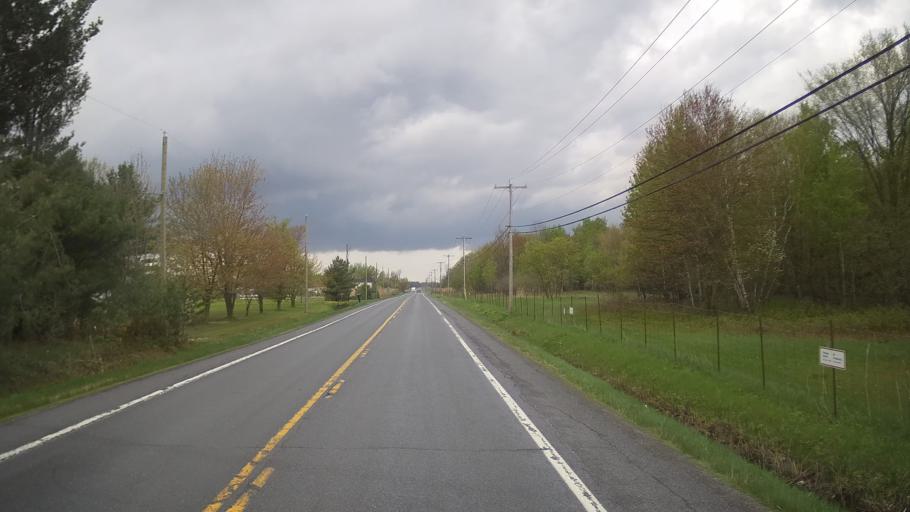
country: CA
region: Quebec
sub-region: Monteregie
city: Farnham
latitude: 45.3066
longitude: -73.0410
